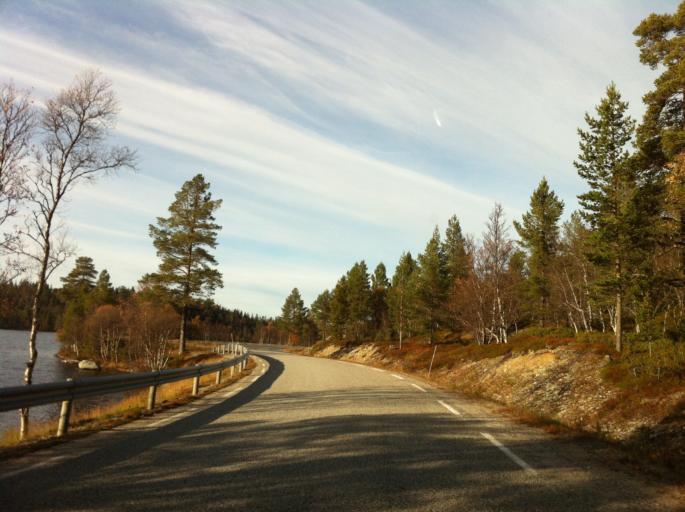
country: NO
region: Hedmark
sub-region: Engerdal
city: Engerdal
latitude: 62.0972
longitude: 12.0315
